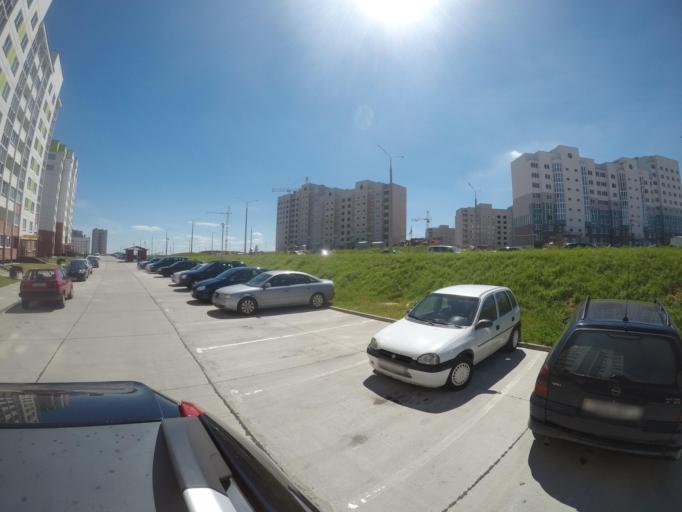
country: BY
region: Grodnenskaya
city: Hrodna
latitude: 53.7201
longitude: 23.8731
